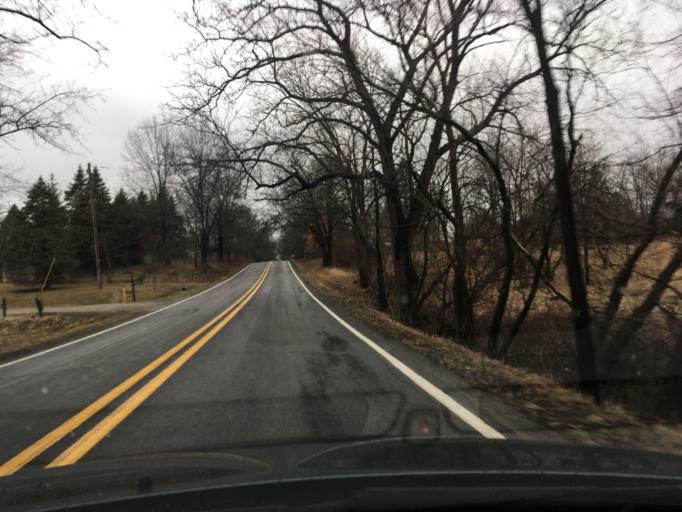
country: US
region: Michigan
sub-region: Washtenaw County
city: Chelsea
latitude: 42.3101
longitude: -84.1199
